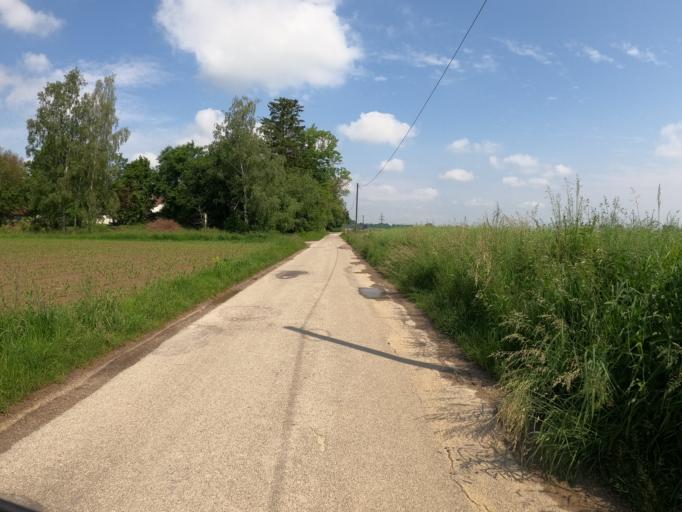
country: DE
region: Bavaria
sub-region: Swabia
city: Holzheim
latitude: 48.3688
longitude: 10.1004
